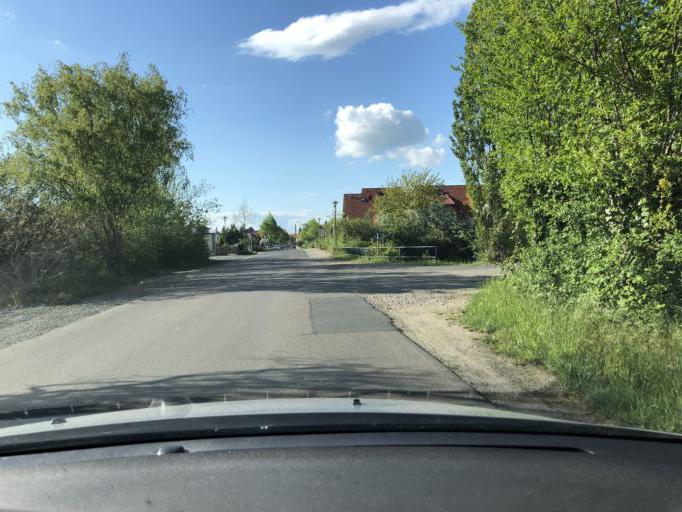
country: DE
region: Saxony
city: Lobstadt
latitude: 51.1276
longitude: 12.4542
